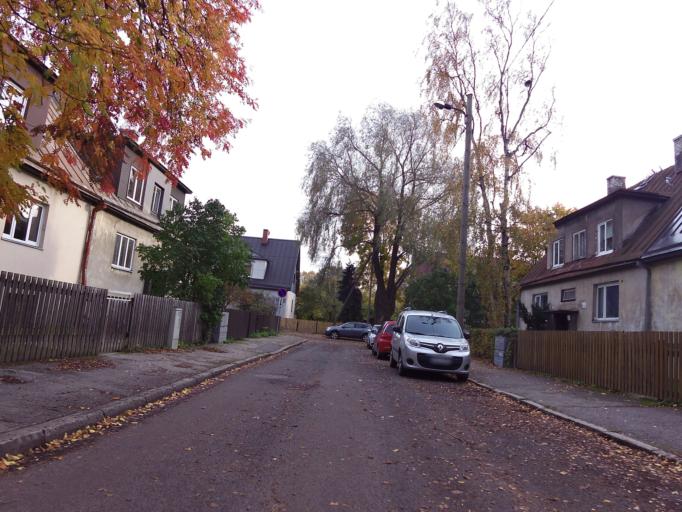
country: EE
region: Harju
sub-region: Tallinna linn
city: Tallinn
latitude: 59.4381
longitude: 24.7114
